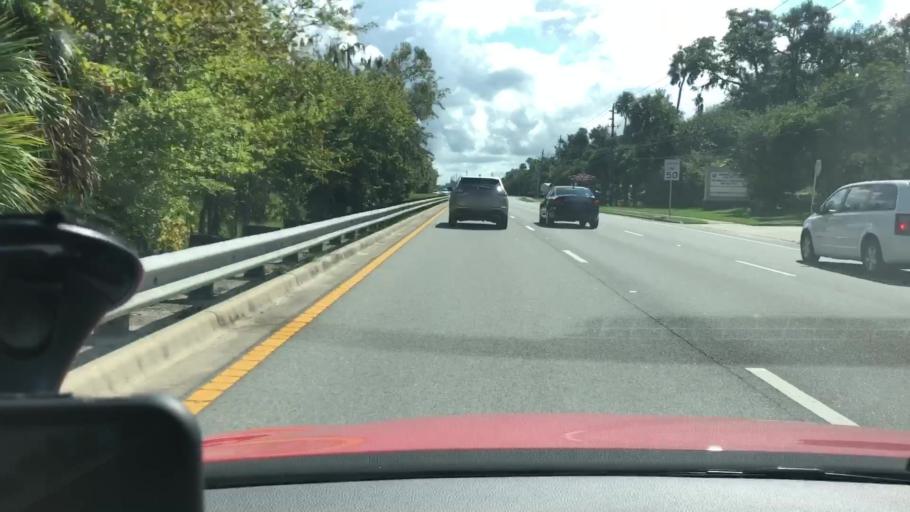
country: US
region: Florida
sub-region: Volusia County
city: Port Orange
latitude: 29.1435
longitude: -81.0139
